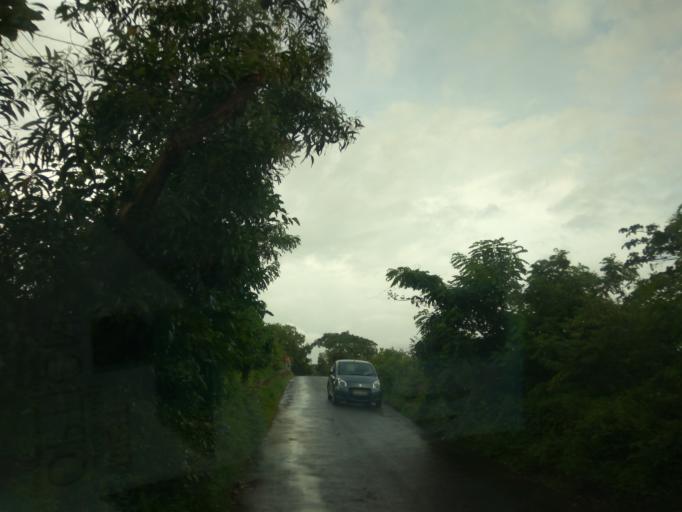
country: IN
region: Goa
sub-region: North Goa
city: Goa Velha
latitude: 15.4431
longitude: 73.8664
